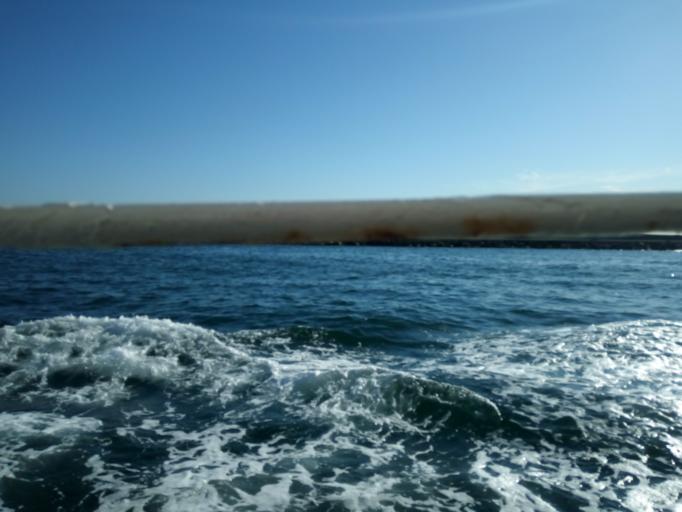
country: TR
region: Istanbul
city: UEskuedar
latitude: 41.0013
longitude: 29.0090
